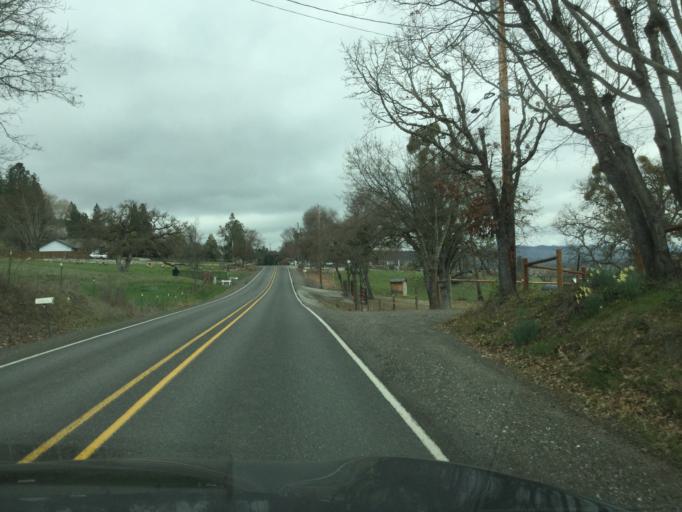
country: US
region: Oregon
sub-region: Jackson County
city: Central Point
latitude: 42.3780
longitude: -122.9584
